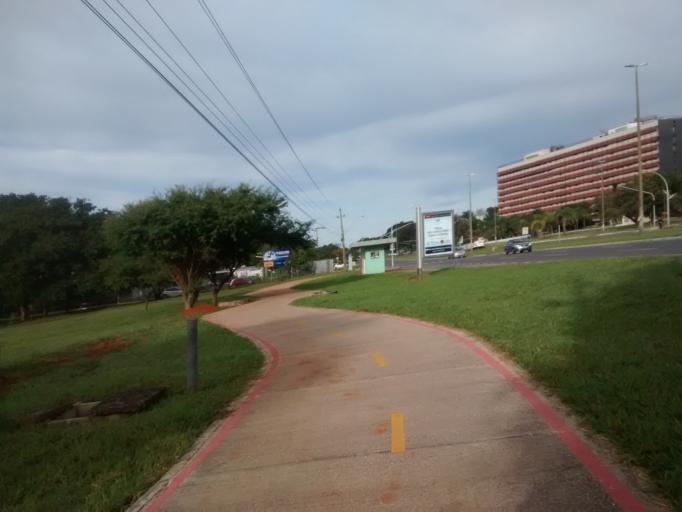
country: BR
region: Federal District
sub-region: Brasilia
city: Brasilia
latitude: -15.8045
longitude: -47.8789
